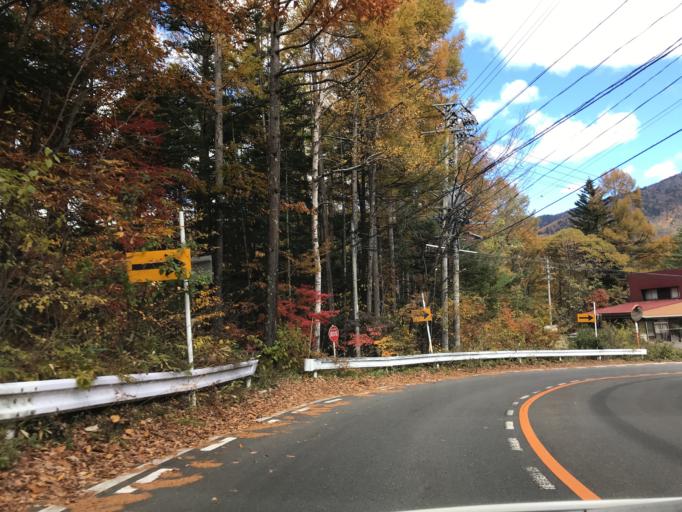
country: JP
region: Nagano
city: Toyoshina
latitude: 36.1375
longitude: 137.6703
